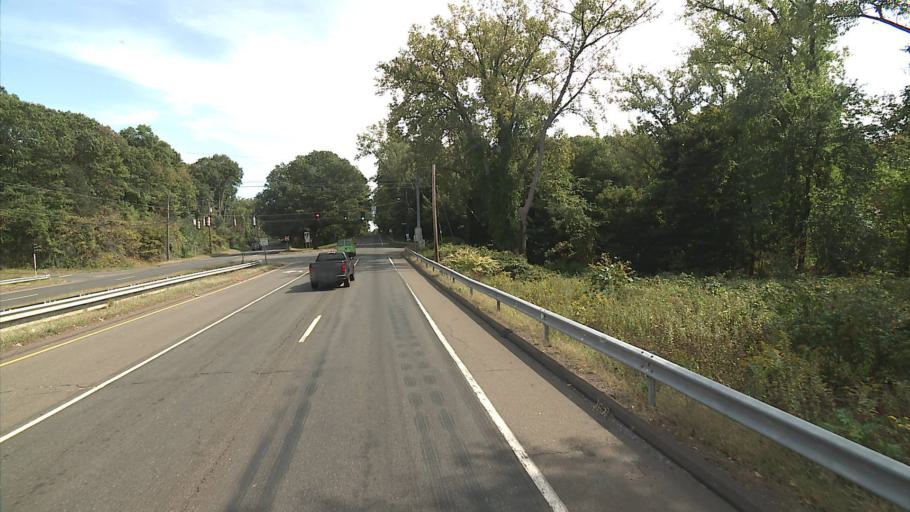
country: US
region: Connecticut
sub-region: New Haven County
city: Orange
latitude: 41.2990
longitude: -72.9965
